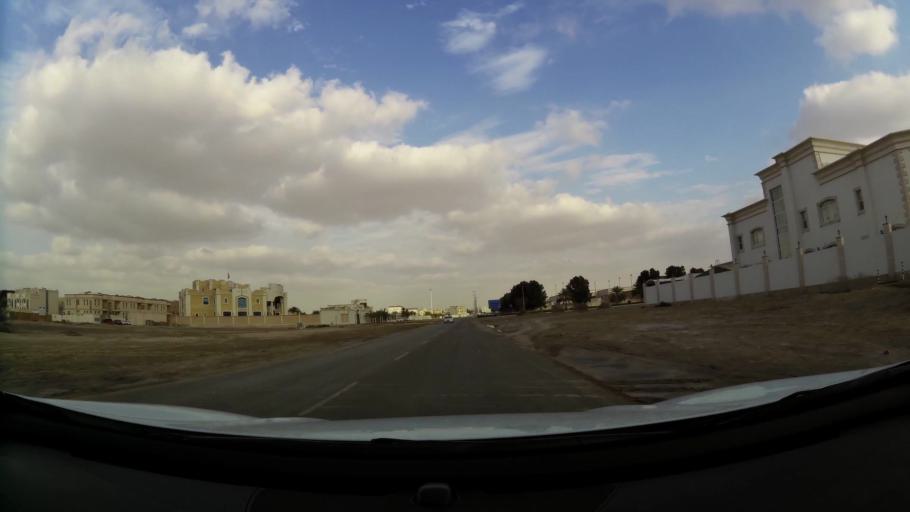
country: AE
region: Abu Dhabi
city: Abu Dhabi
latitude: 24.3638
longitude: 54.5470
